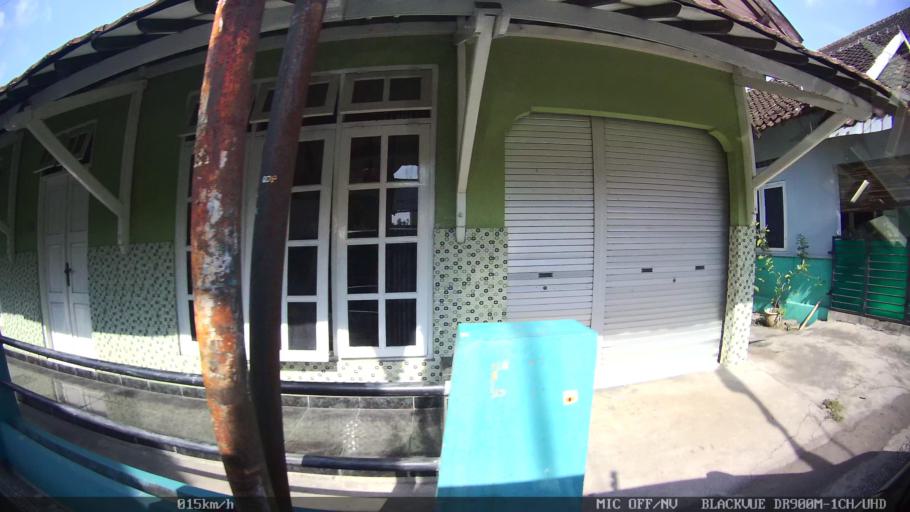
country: ID
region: Daerah Istimewa Yogyakarta
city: Sewon
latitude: -7.8327
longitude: 110.3992
